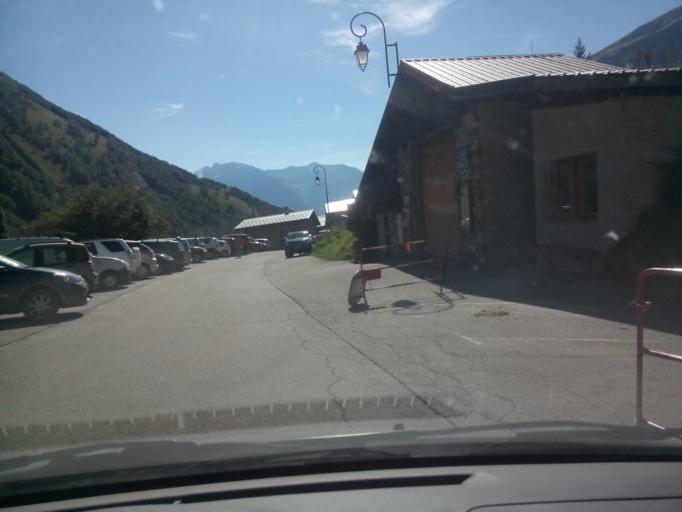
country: FR
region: Rhone-Alpes
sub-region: Departement de l'Isere
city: Mont-de-Lans
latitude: 45.0730
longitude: 6.1741
